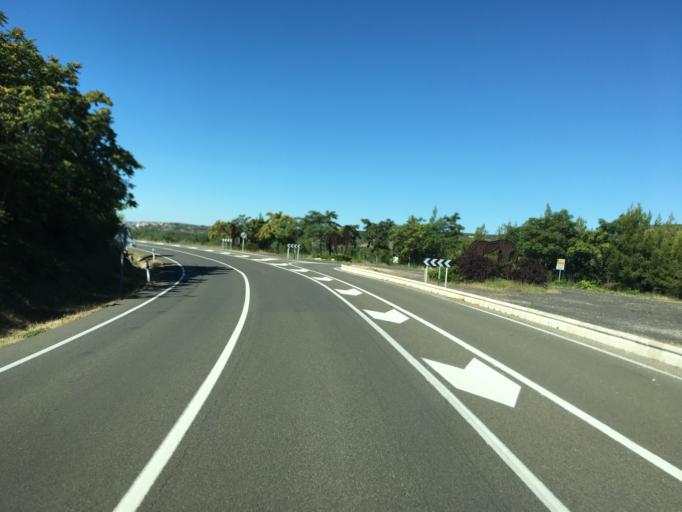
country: ES
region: Aragon
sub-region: Provincia de Huesca
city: Estada
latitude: 42.1009
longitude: 0.2441
